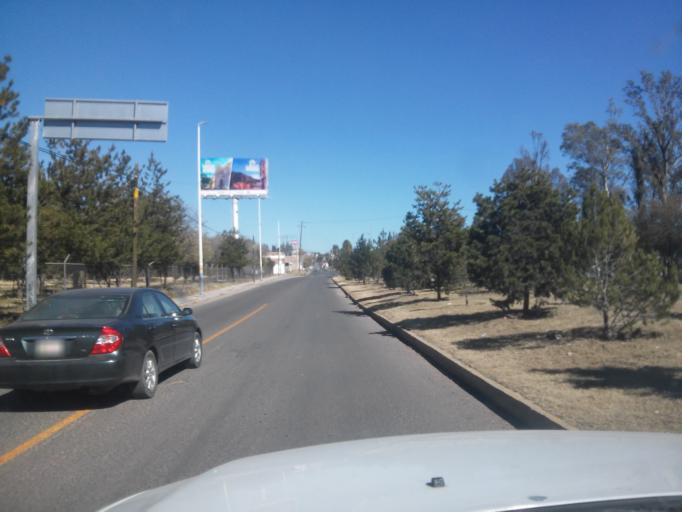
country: MX
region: Durango
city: Victoria de Durango
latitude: 24.0262
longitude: -104.6917
